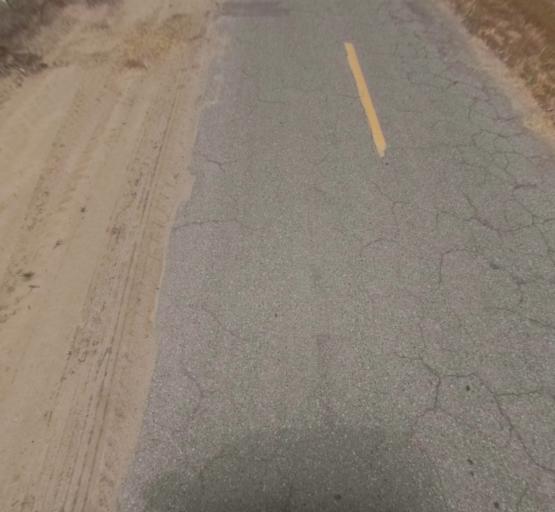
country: US
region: California
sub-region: Madera County
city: Fairmead
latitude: 37.0037
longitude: -120.2234
